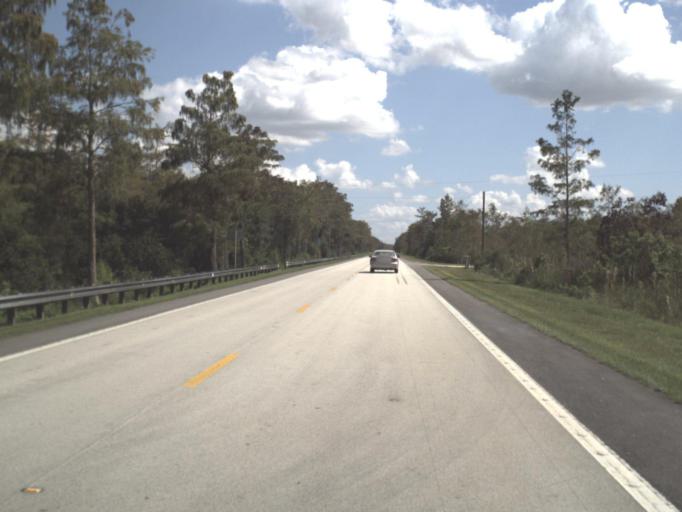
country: US
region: Florida
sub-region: Miami-Dade County
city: Kendall West
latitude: 25.8183
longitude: -80.8882
